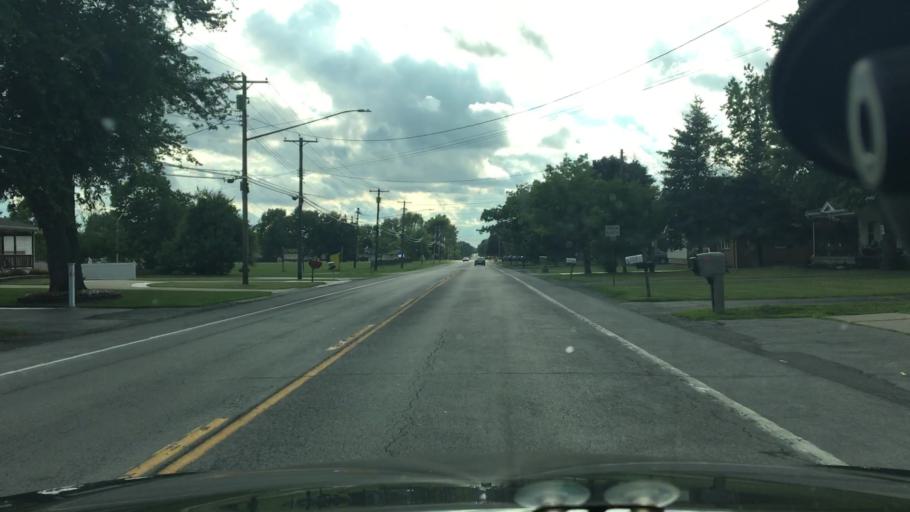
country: US
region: New York
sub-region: Erie County
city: Cheektowaga
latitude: 42.8393
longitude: -78.7268
